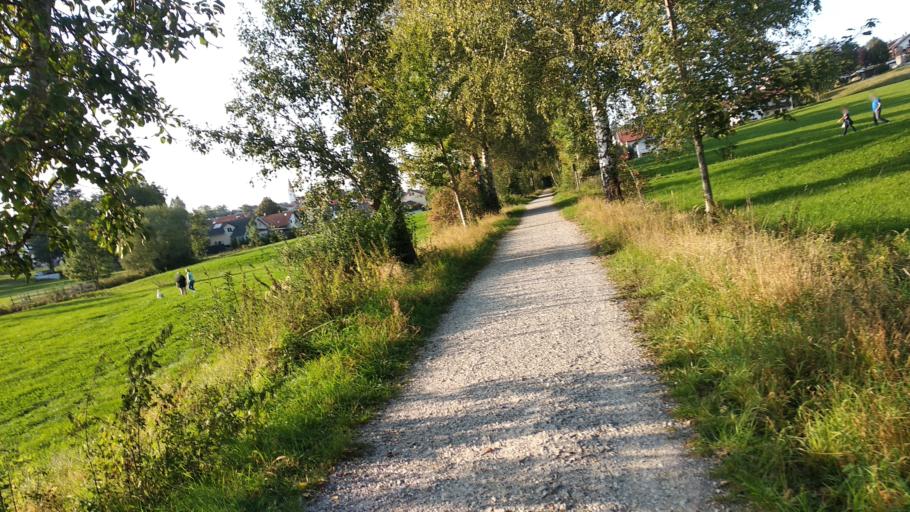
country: DE
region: Bavaria
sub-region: Upper Bavaria
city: Isen
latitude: 48.2069
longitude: 12.0643
